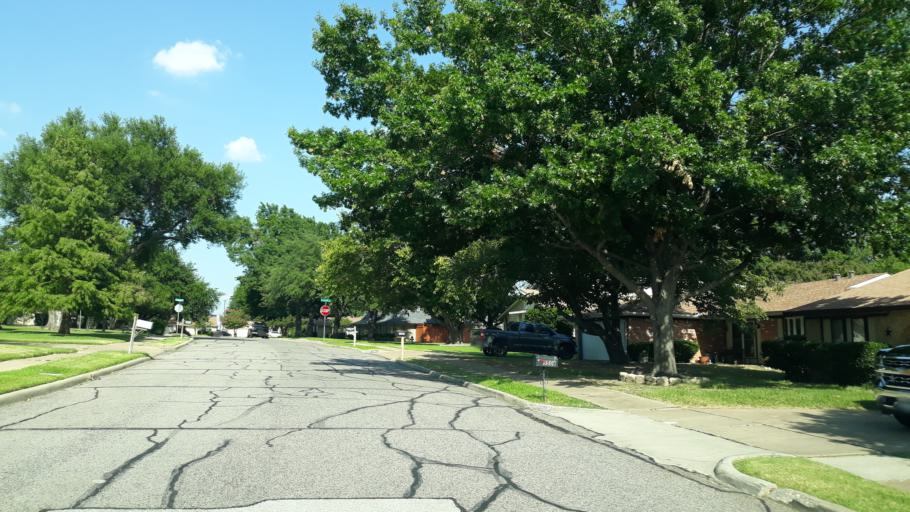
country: US
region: Texas
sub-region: Dallas County
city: Irving
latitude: 32.8450
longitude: -96.9962
